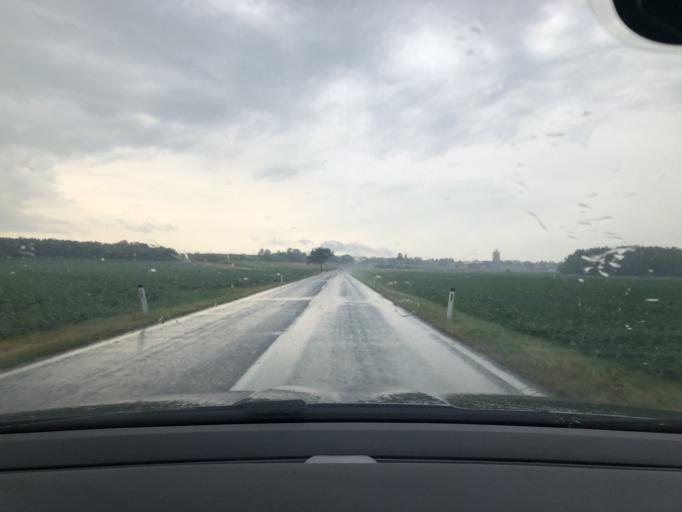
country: AT
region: Lower Austria
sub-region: Politischer Bezirk Ganserndorf
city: Marchegg
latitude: 48.3072
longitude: 16.8518
